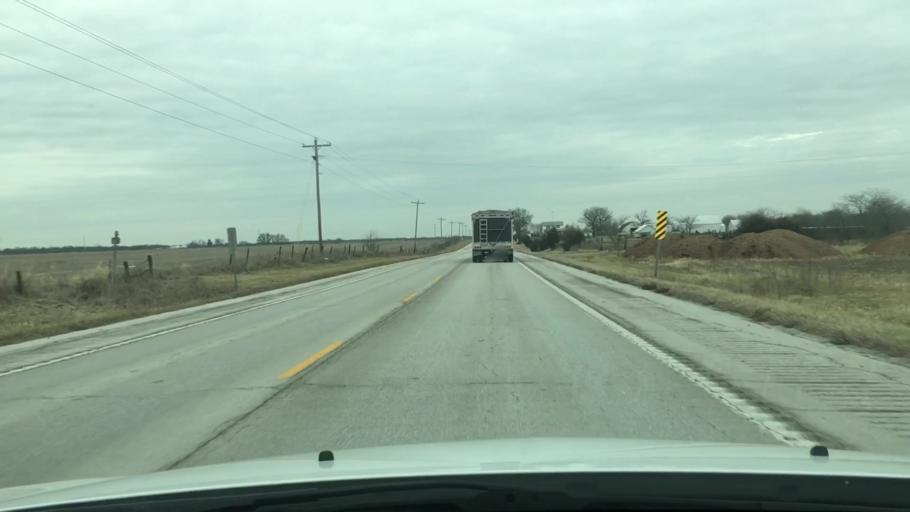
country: US
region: Missouri
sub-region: Montgomery County
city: Wellsville
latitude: 39.1731
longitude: -91.6476
